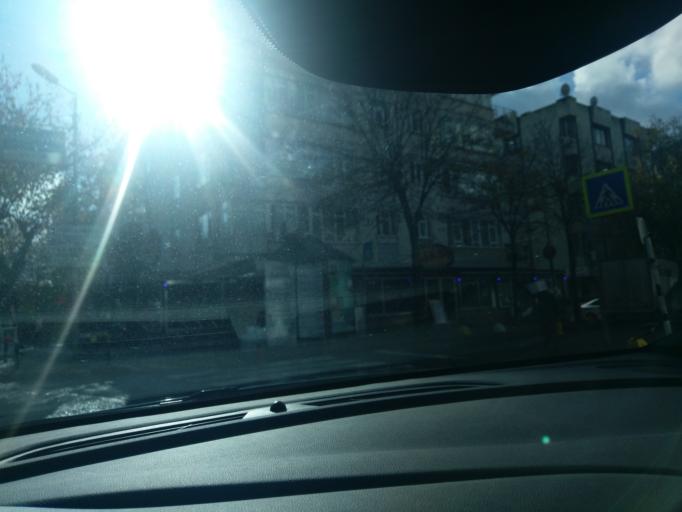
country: TR
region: Istanbul
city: Sisli
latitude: 41.0653
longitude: 28.9958
